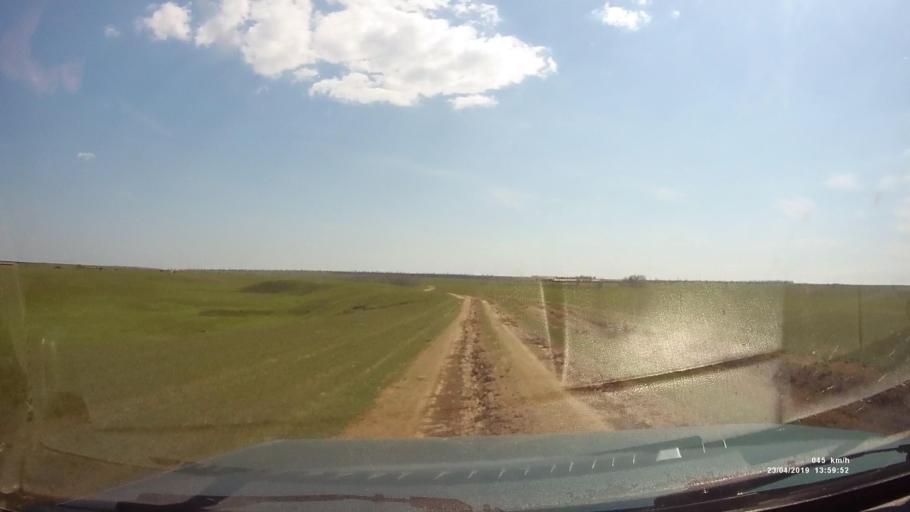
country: RU
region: Rostov
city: Remontnoye
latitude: 46.5636
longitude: 42.9469
